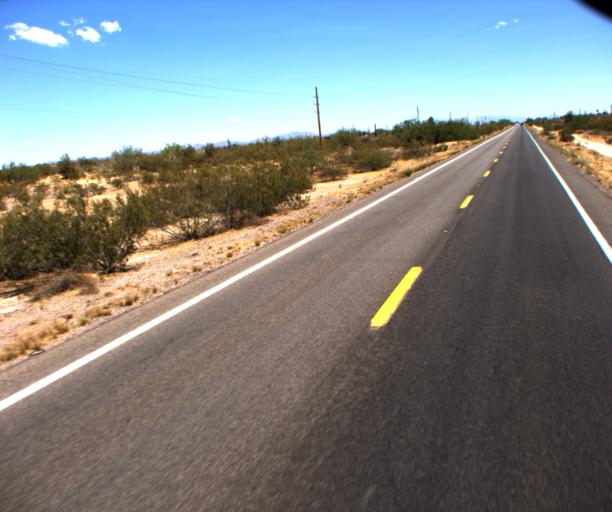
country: US
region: Arizona
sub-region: Pinal County
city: Florence
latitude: 32.9705
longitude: -111.3451
